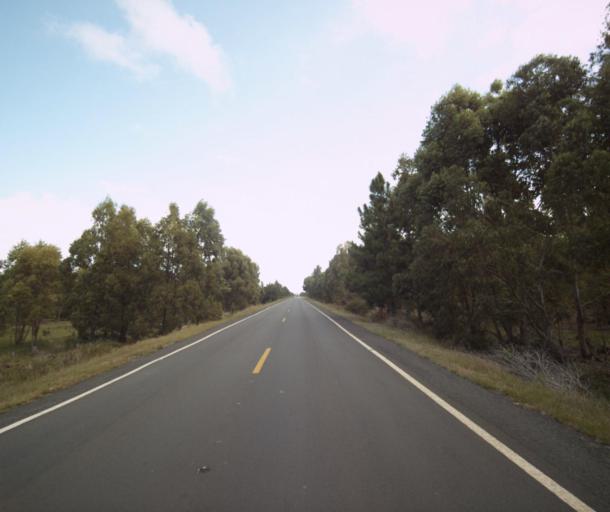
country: BR
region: Rio Grande do Sul
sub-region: Tapes
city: Tapes
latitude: -31.4301
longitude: -51.1884
